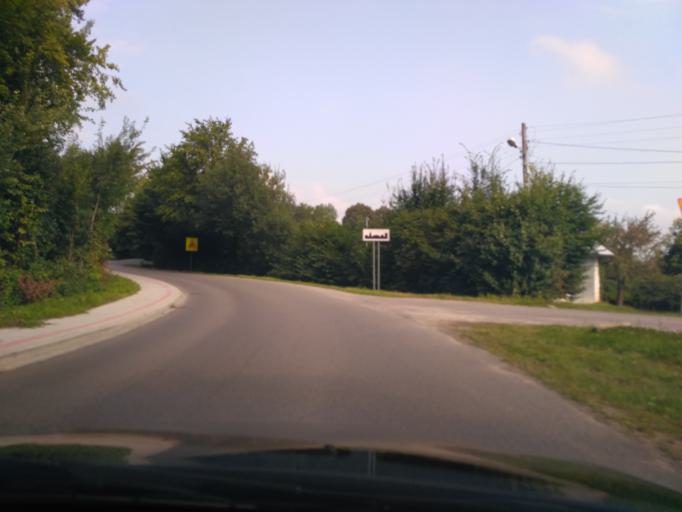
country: PL
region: Subcarpathian Voivodeship
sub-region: Powiat strzyzowski
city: Czudec
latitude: 49.9706
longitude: 21.8371
